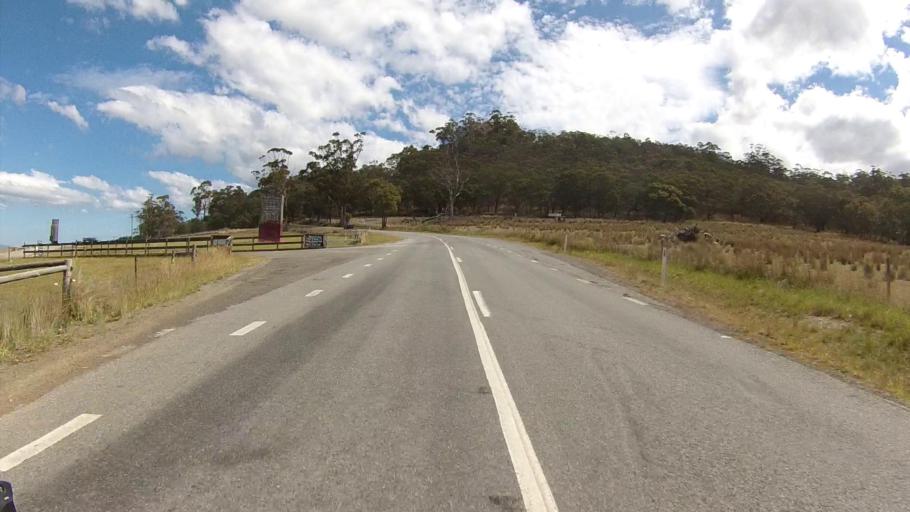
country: AU
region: Tasmania
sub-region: Break O'Day
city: St Helens
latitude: -41.9705
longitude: 148.1514
